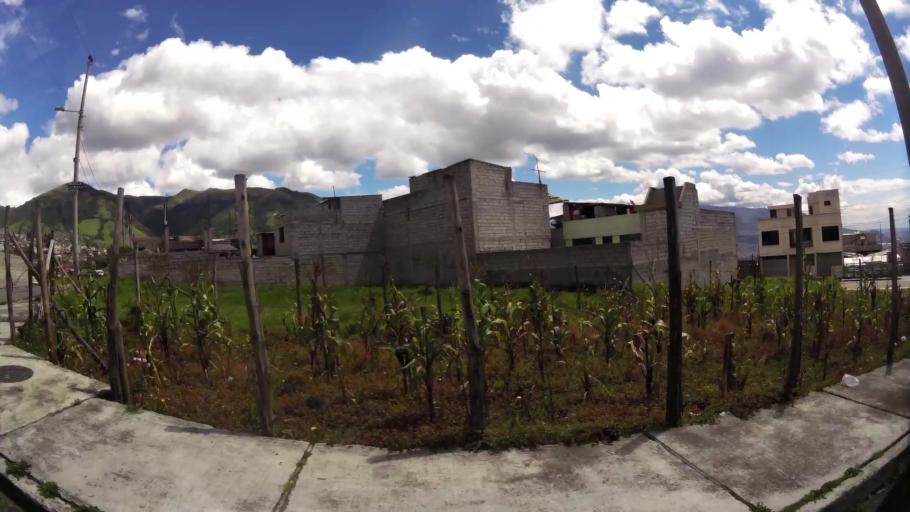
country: EC
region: Pichincha
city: Quito
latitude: -0.3333
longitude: -78.5639
